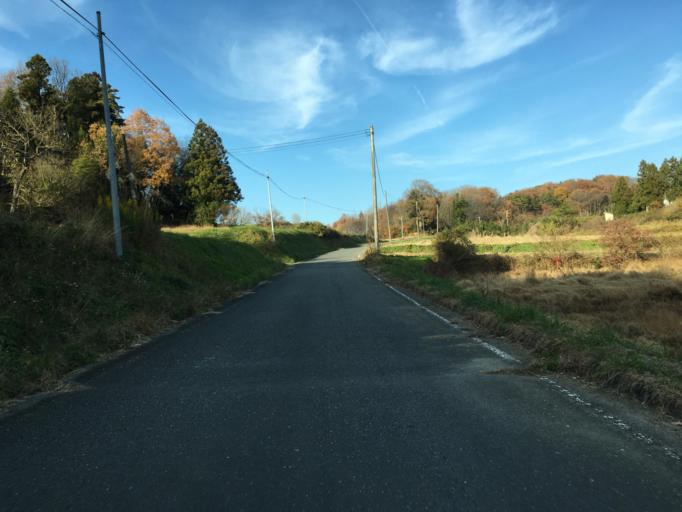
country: JP
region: Fukushima
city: Ishikawa
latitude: 37.2538
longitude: 140.5686
